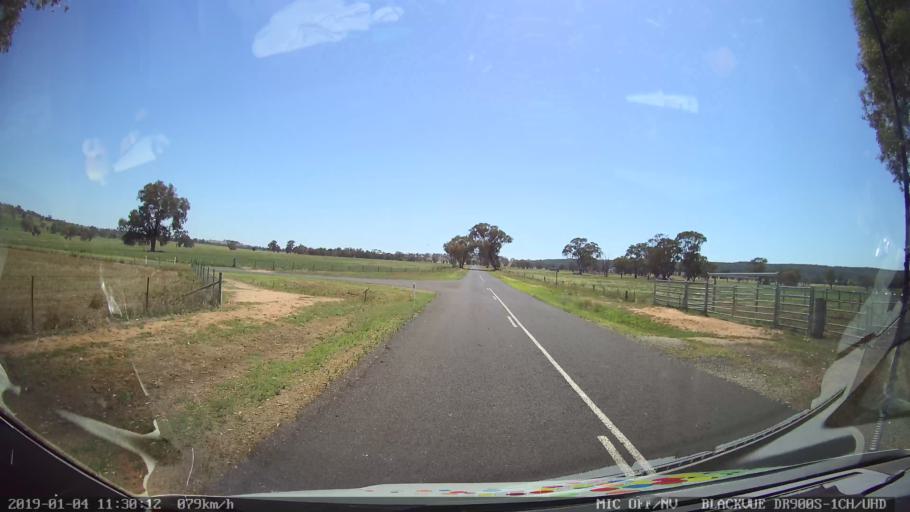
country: AU
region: New South Wales
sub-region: Cabonne
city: Molong
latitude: -33.0796
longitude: 148.7786
